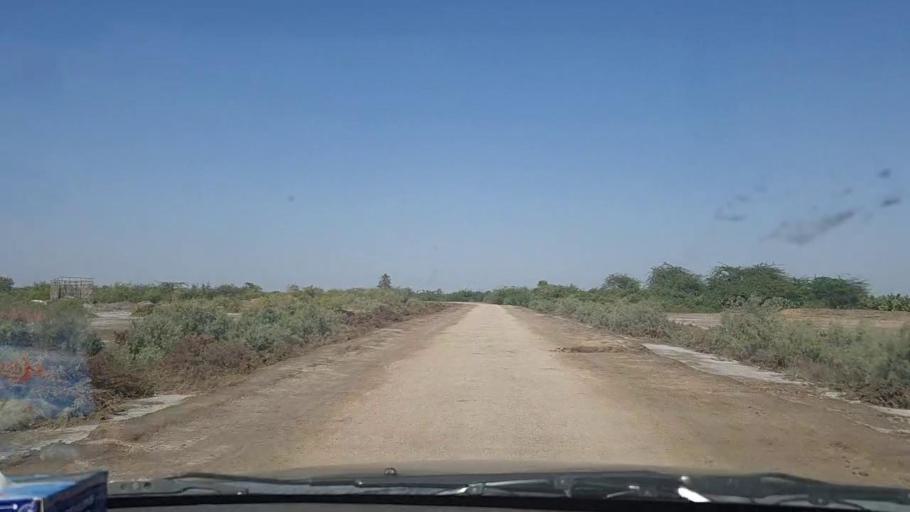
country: PK
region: Sindh
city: Chuhar Jamali
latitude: 24.2770
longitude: 67.7622
